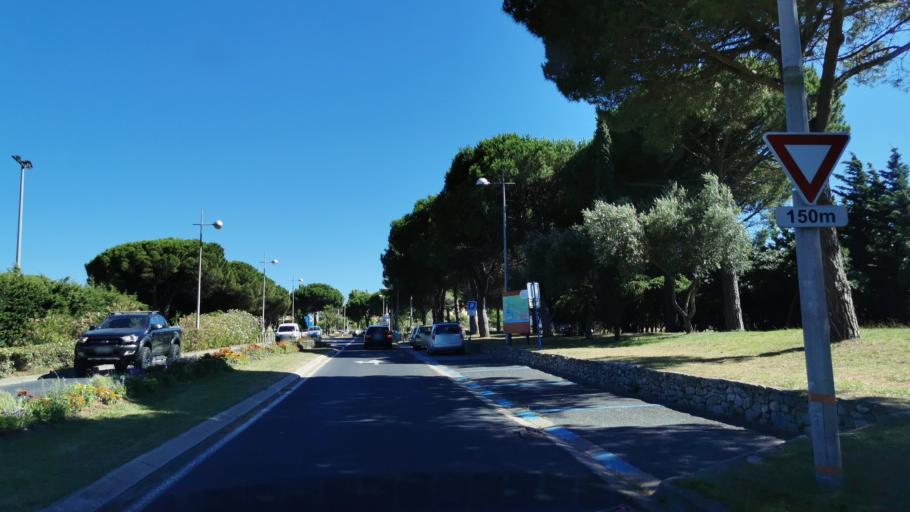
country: FR
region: Languedoc-Roussillon
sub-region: Departement de l'Aude
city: Gruissan
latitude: 43.1136
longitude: 3.0929
